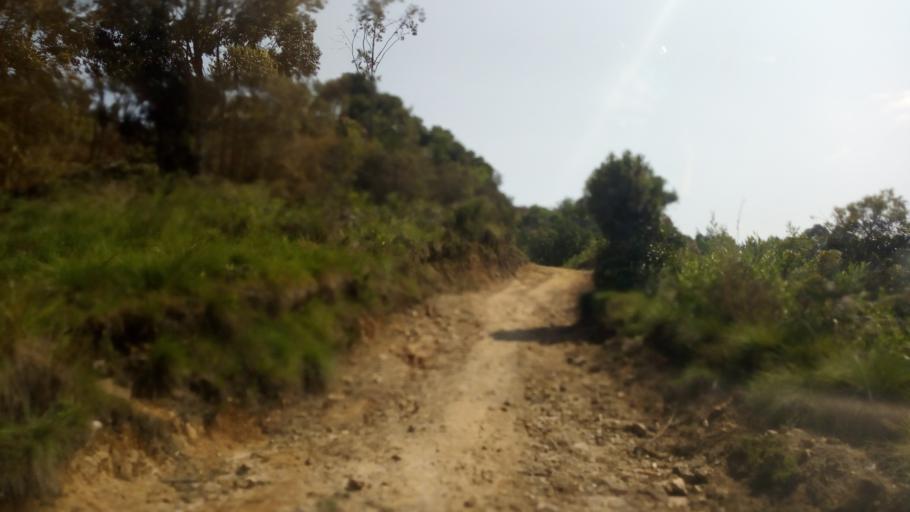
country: UG
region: Western Region
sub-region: Kisoro District
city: Kisoro
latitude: -1.0964
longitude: 29.5853
